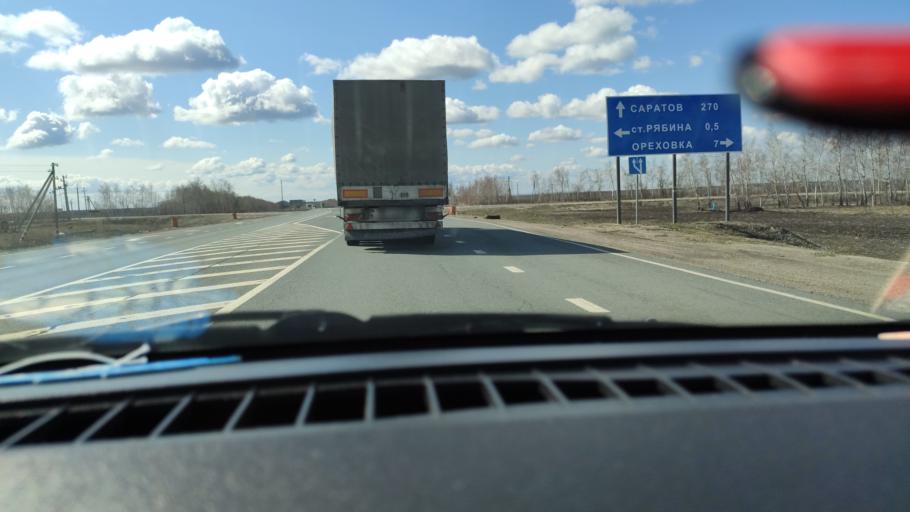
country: RU
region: Samara
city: Syzran'
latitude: 52.9228
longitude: 48.3032
